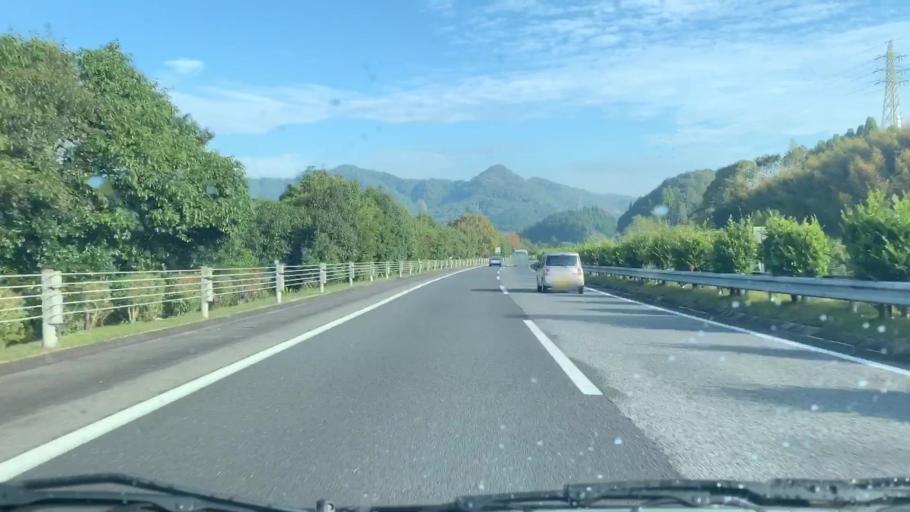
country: JP
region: Saga Prefecture
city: Takeocho-takeo
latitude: 33.2249
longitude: 130.0503
